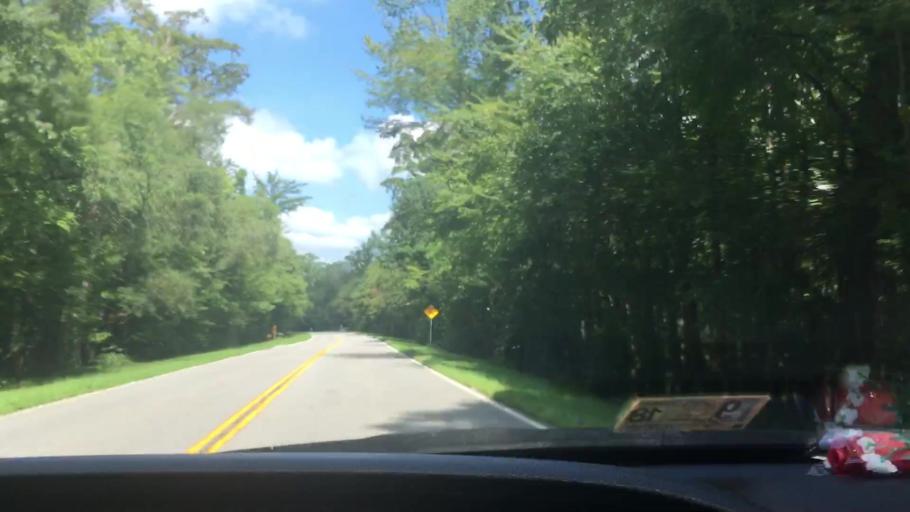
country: US
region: Virginia
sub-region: City of Virginia Beach
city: Virginia Beach
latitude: 36.7433
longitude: -76.1148
